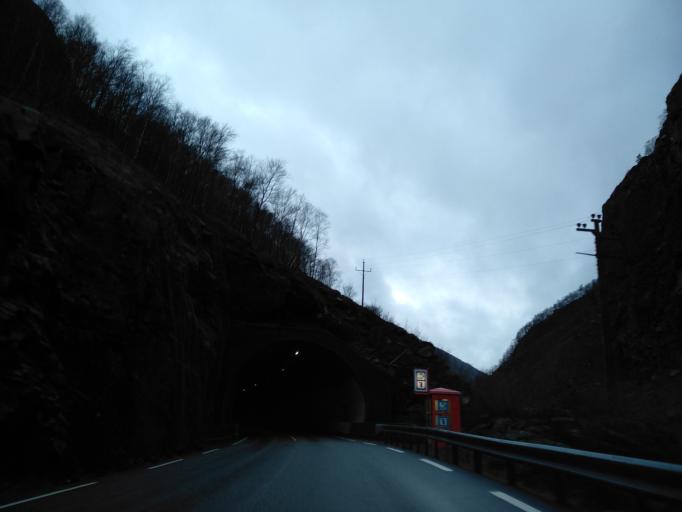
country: NO
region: Rogaland
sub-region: Forsand
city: Forsand
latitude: 58.7869
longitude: 6.2892
